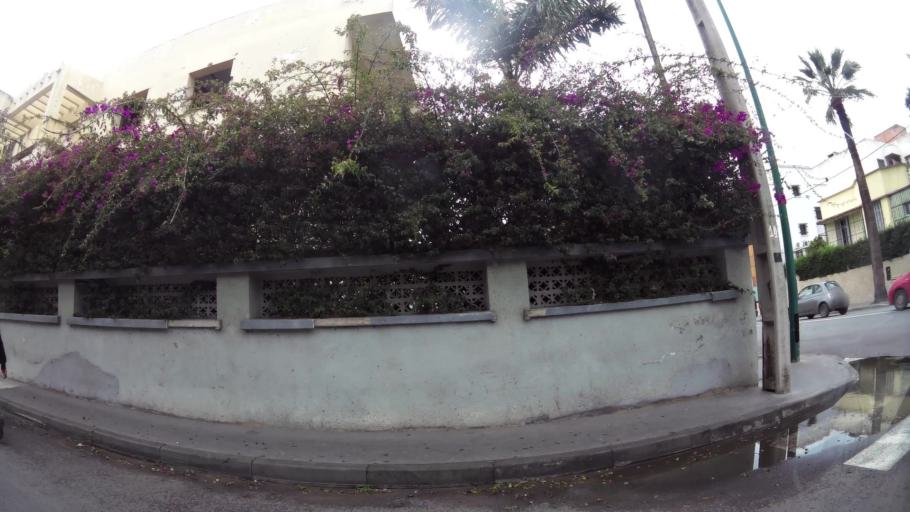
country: MA
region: Grand Casablanca
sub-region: Casablanca
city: Casablanca
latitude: 33.5807
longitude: -7.6093
